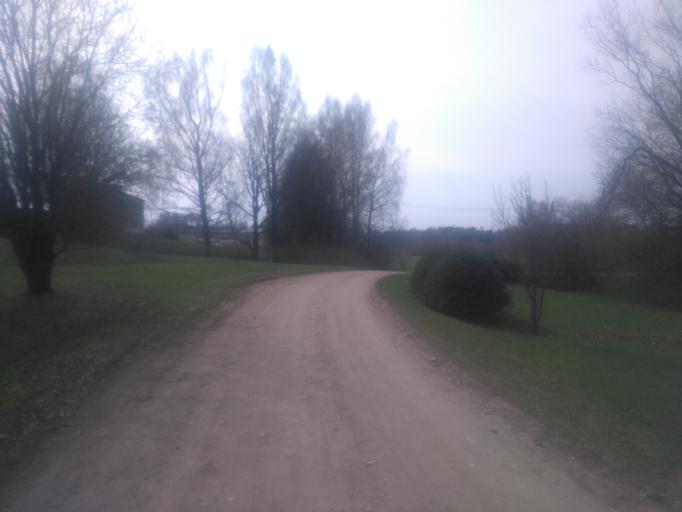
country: LV
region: Vecpiebalga
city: Vecpiebalga
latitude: 57.0244
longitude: 25.8474
